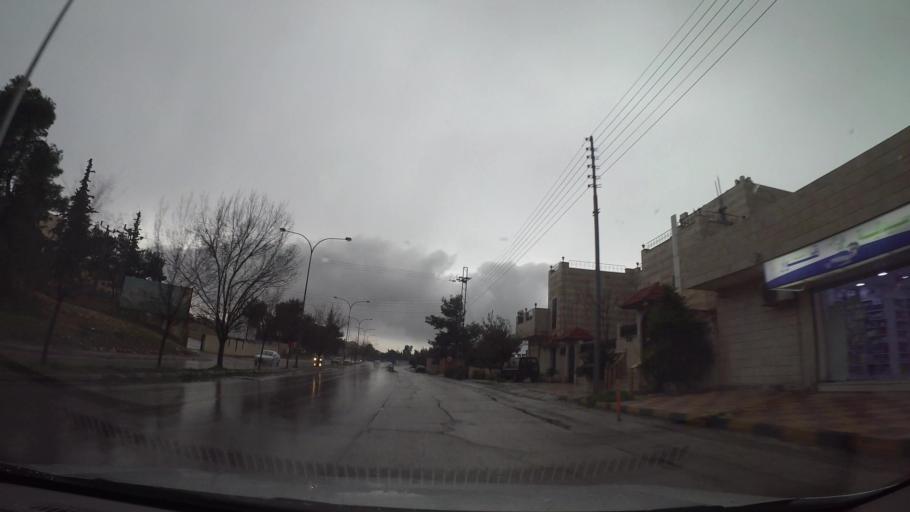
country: JO
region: Amman
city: Umm as Summaq
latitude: 31.8953
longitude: 35.8530
